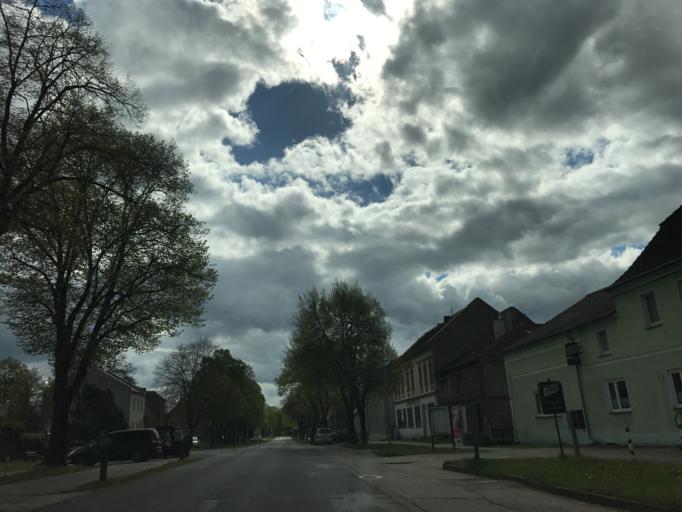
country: DE
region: Brandenburg
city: Roskow
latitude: 52.4726
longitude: 12.7143
